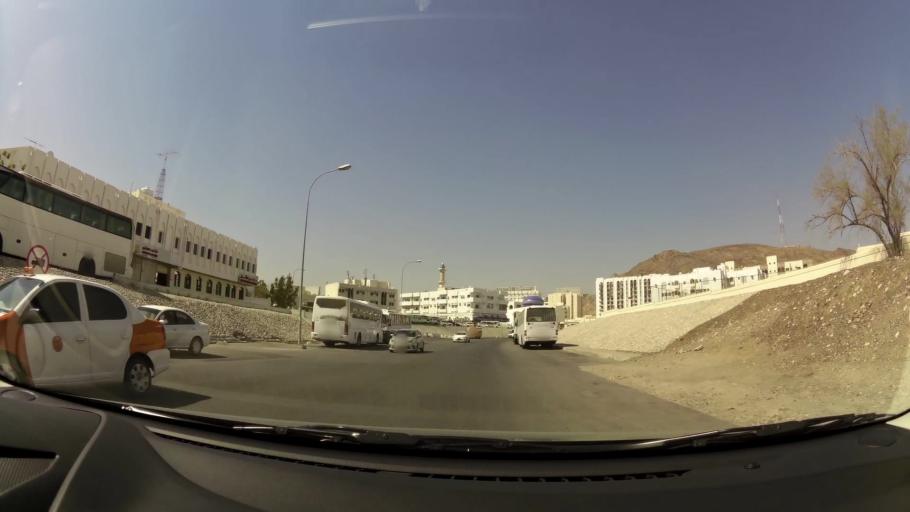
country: OM
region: Muhafazat Masqat
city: Muscat
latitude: 23.5980
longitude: 58.5446
